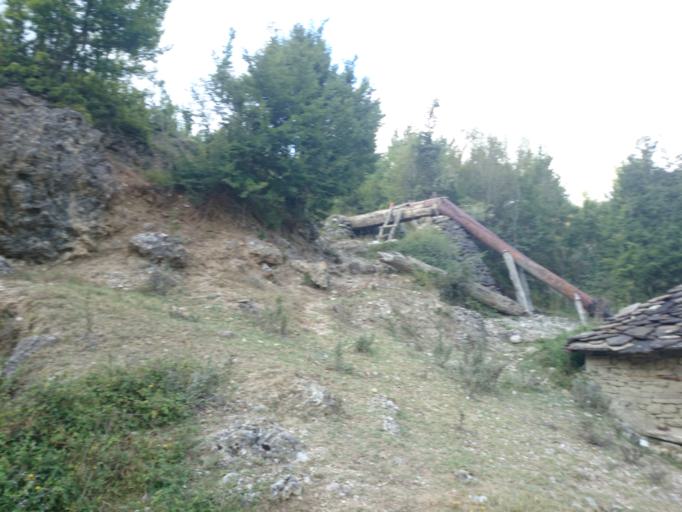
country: AL
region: Elbasan
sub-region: Rrethi i Gramshit
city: Porocan
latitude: 40.9347
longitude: 20.2692
